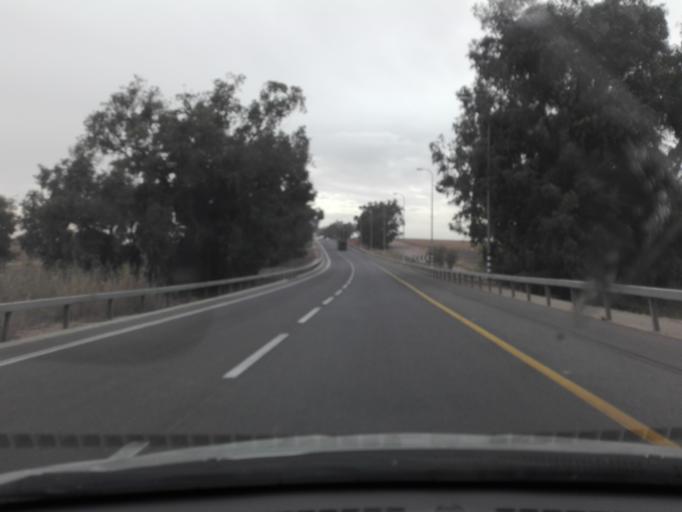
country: IL
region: Southern District
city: Lehavim
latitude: 31.4869
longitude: 34.7772
